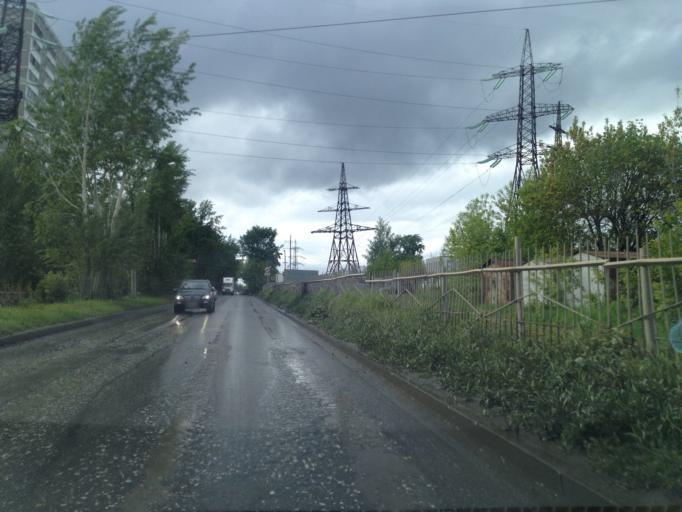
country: RU
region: Sverdlovsk
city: Yekaterinburg
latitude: 56.8721
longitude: 60.5600
